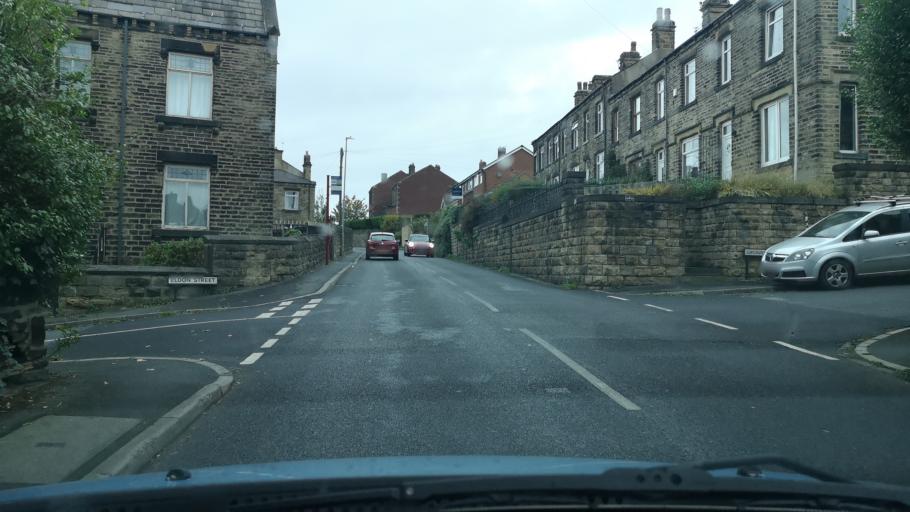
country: GB
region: England
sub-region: Kirklees
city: Heckmondwike
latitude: 53.7115
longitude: -1.6739
